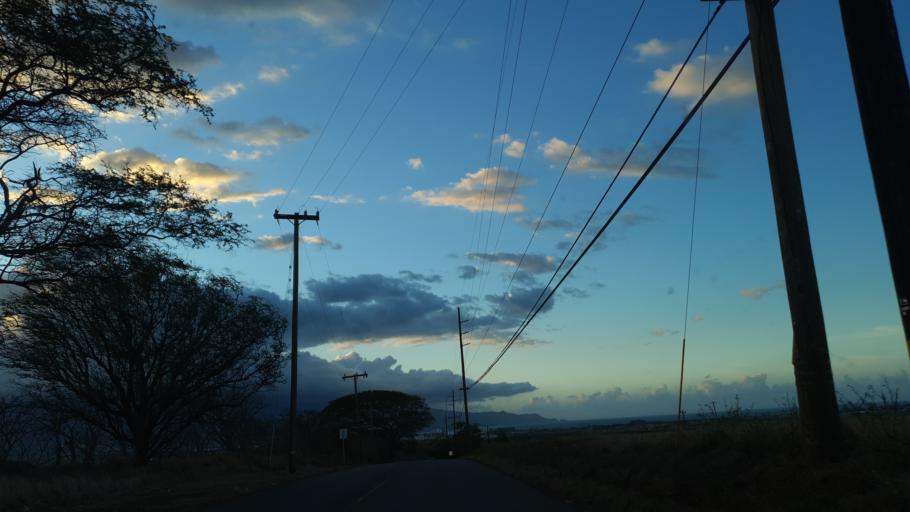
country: US
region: Hawaii
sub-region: Maui County
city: Kahului
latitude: 20.8642
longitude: -156.4305
